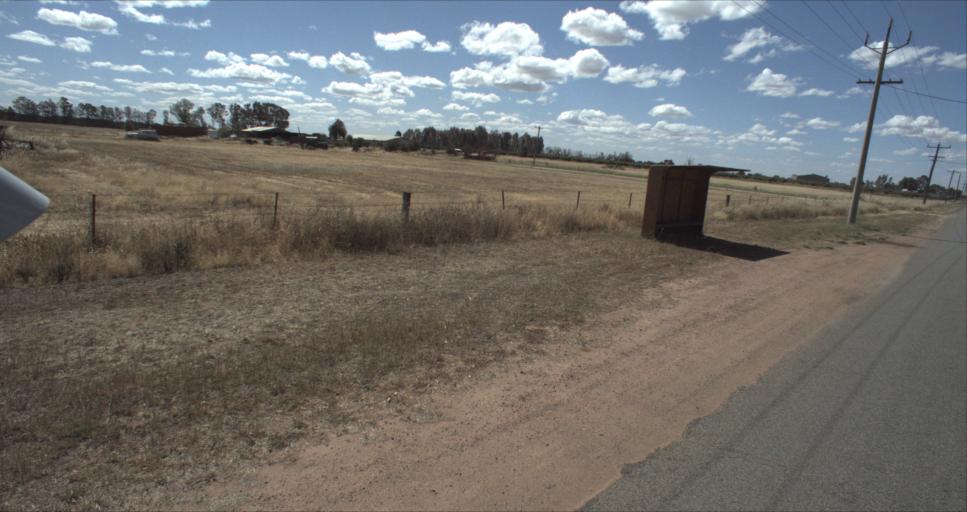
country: AU
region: New South Wales
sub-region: Leeton
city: Leeton
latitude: -34.5141
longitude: 146.2513
